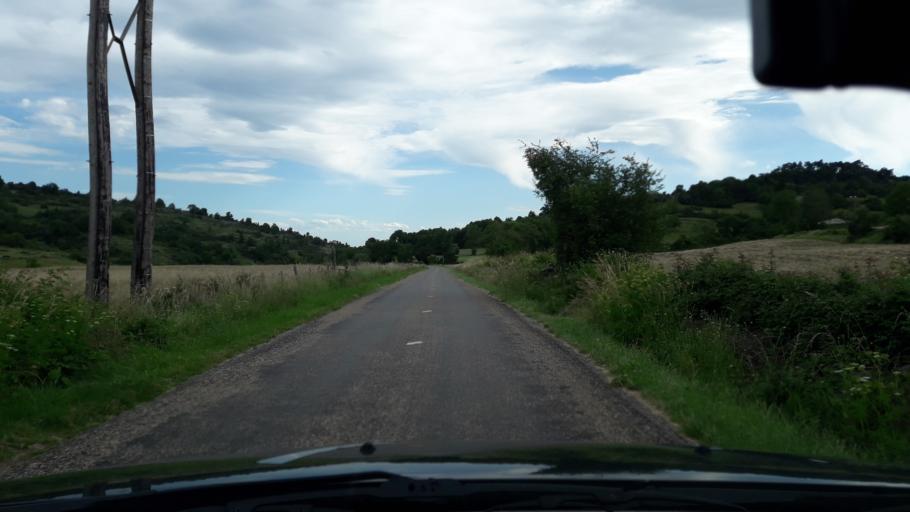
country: FR
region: Rhone-Alpes
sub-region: Departement de l'Ardeche
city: Saint-Priest
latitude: 44.6811
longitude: 4.5385
